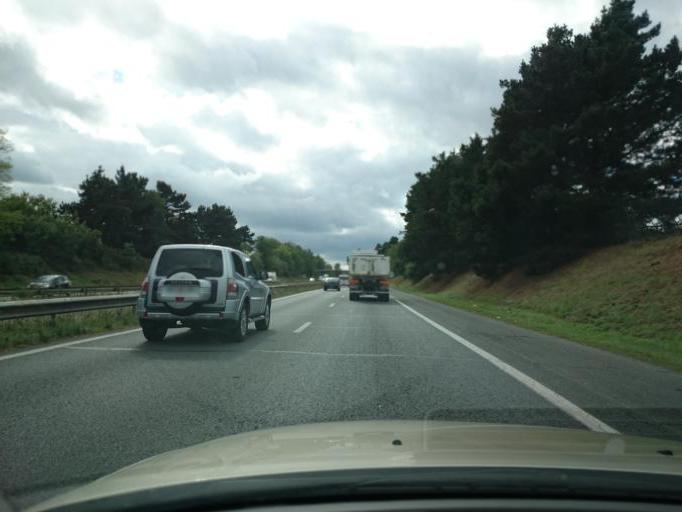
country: FR
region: Aquitaine
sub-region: Departement de la Gironde
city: Eysines
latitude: 44.8739
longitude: -0.6380
